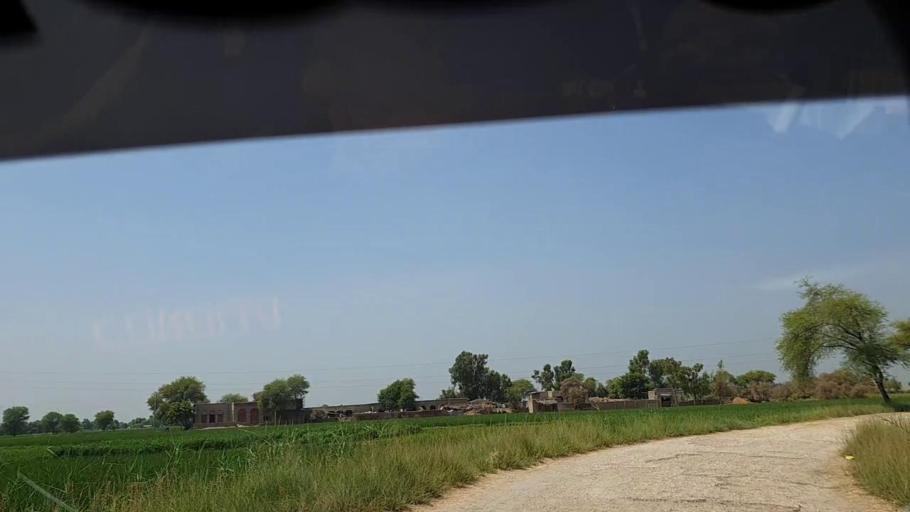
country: PK
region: Sindh
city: Ghauspur
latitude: 28.1728
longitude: 69.0685
